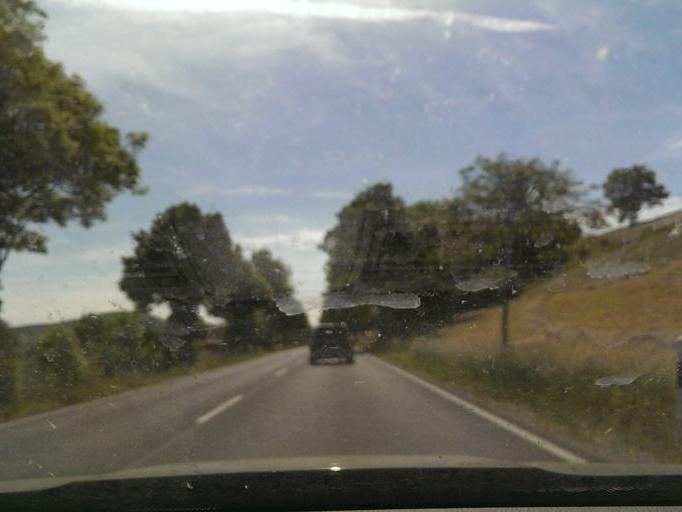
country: DE
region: Lower Saxony
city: Bruggen
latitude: 52.0154
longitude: 9.7833
